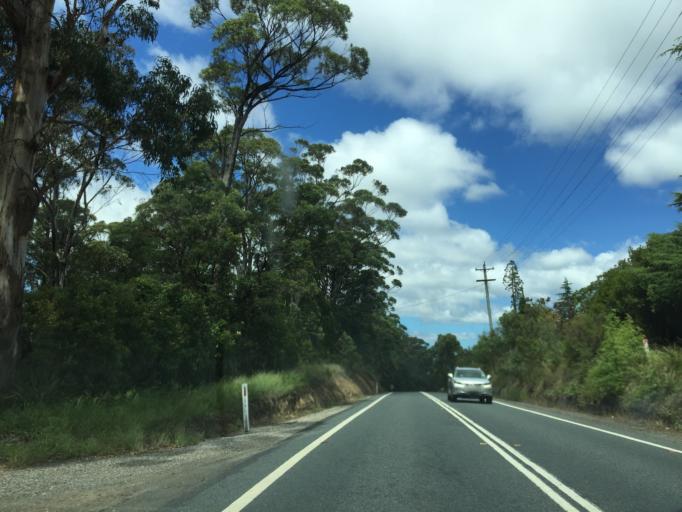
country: AU
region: New South Wales
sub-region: Blue Mountains Municipality
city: Hazelbrook
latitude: -33.5125
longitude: 150.4925
